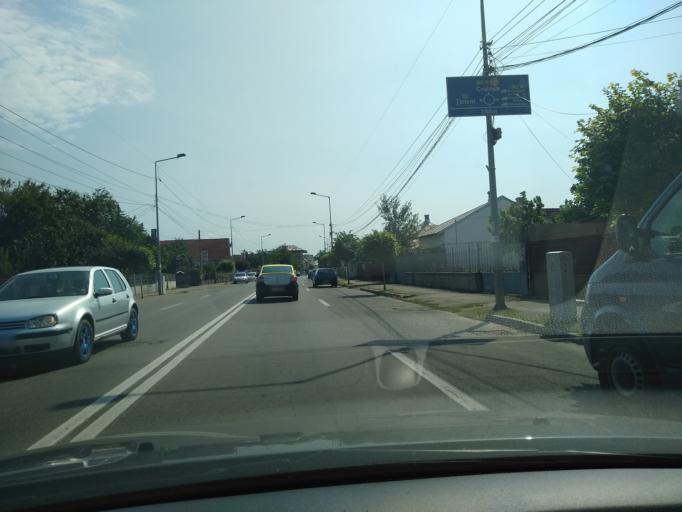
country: RO
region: Gorj
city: Targu Jiu
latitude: 45.0194
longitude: 23.2681
